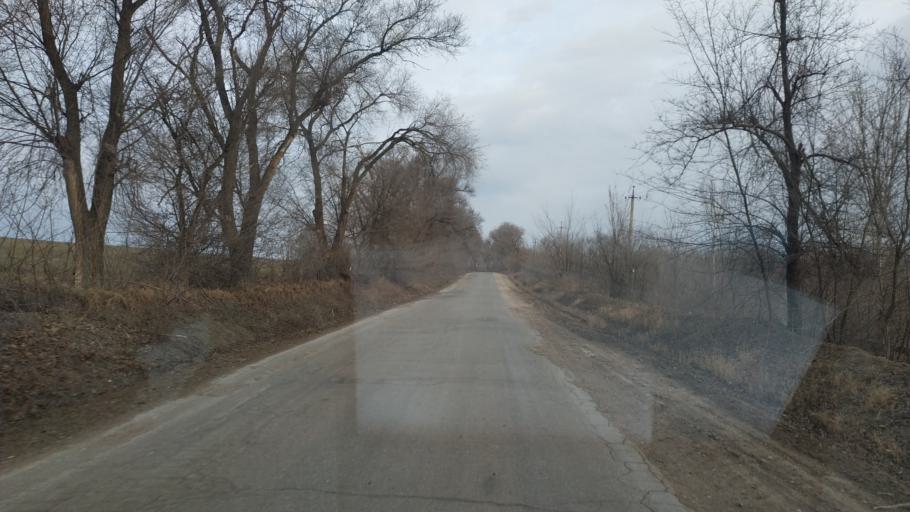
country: MD
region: Chisinau
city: Singera
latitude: 46.9305
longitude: 29.0479
